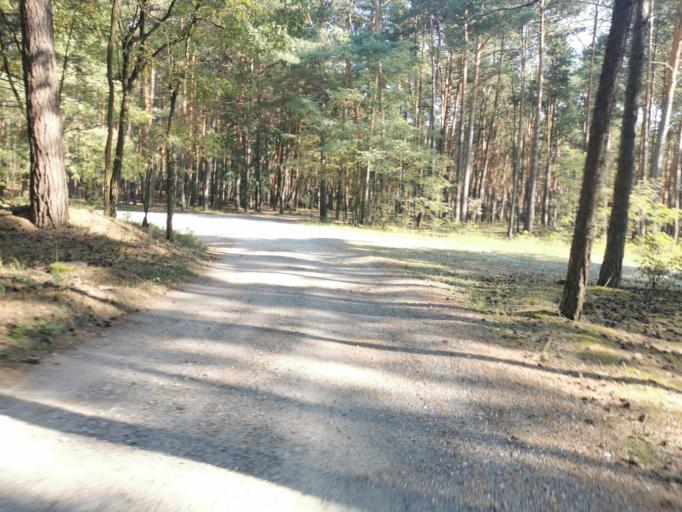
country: SK
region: Trnavsky
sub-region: Okres Senica
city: Senica
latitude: 48.6428
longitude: 17.2434
